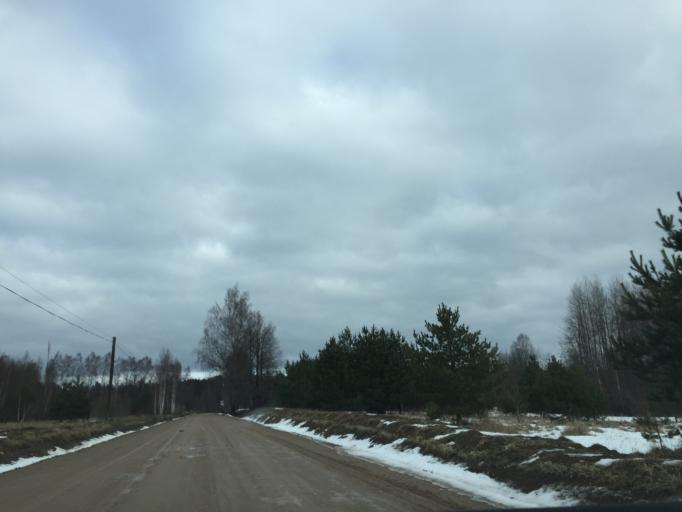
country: LV
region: Salacgrivas
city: Ainazi
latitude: 57.8570
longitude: 24.4979
